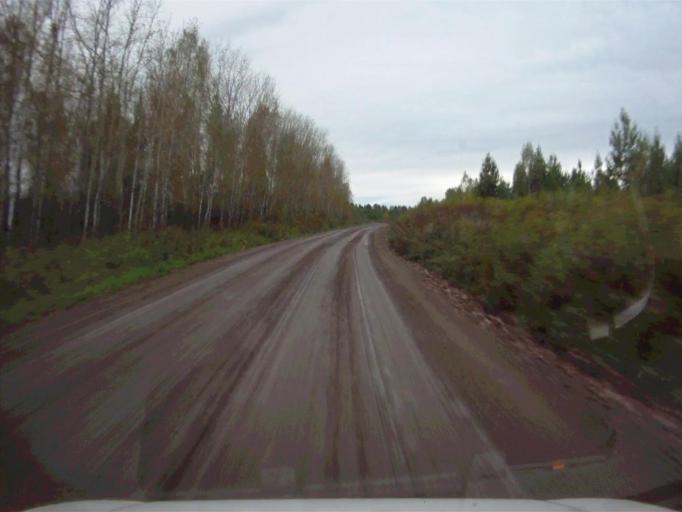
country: RU
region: Chelyabinsk
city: Nyazepetrovsk
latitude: 56.1369
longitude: 59.3012
